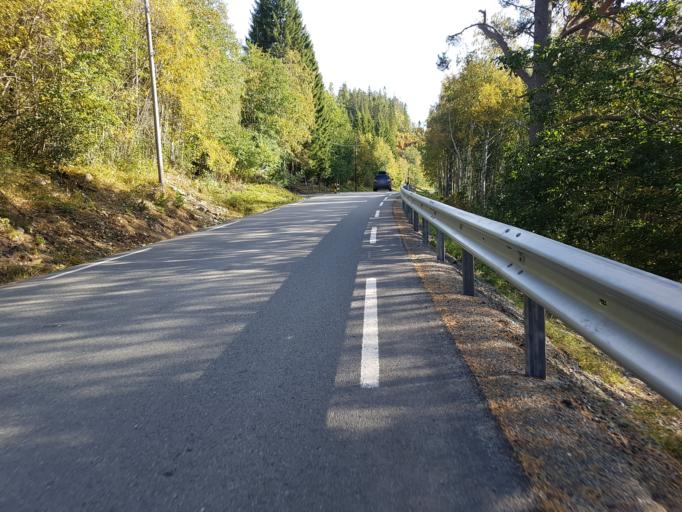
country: NO
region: Sor-Trondelag
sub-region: Malvik
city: Malvik
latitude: 63.3676
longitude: 10.6200
